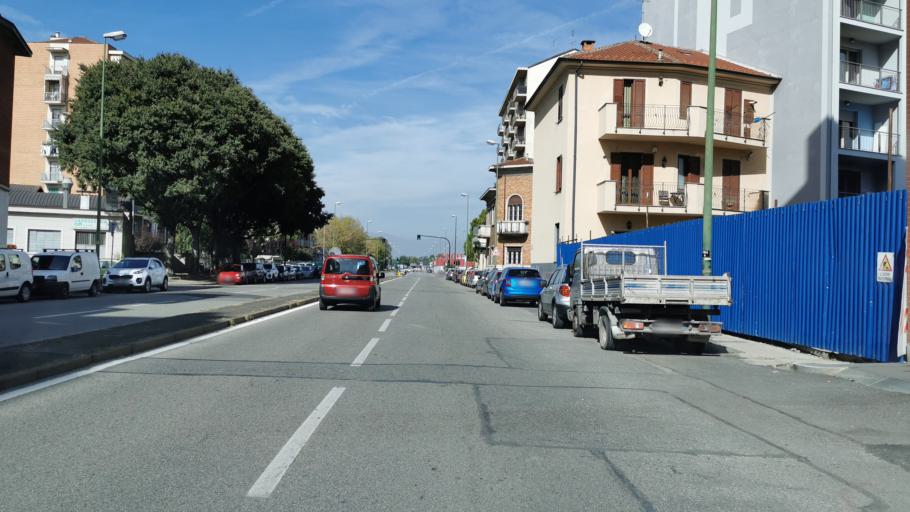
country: IT
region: Piedmont
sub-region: Provincia di Torino
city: Venaria Reale
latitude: 45.1072
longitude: 7.6634
